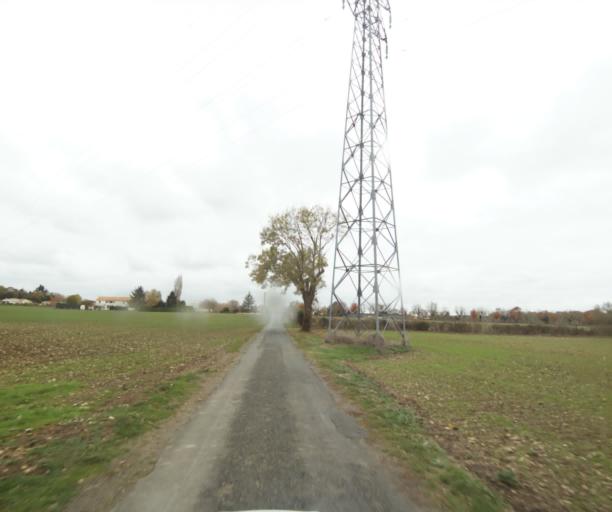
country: FR
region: Poitou-Charentes
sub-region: Departement de la Charente-Maritime
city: Saintes
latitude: 45.7663
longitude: -0.6300
